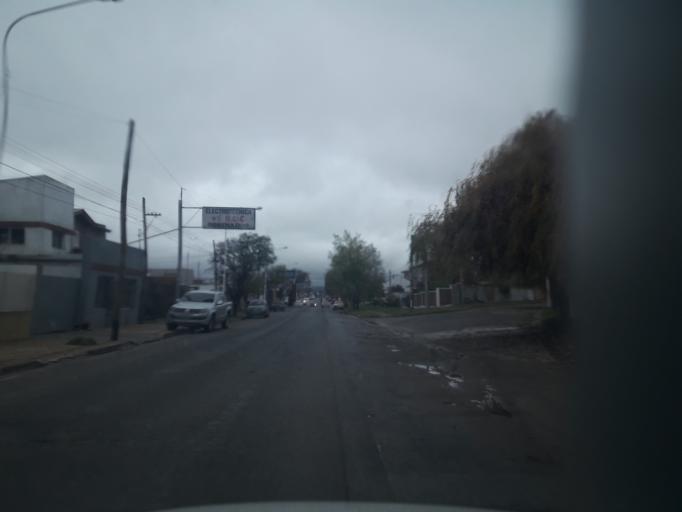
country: AR
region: Buenos Aires
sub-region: Partido de Tandil
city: Tandil
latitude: -37.3112
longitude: -59.1565
